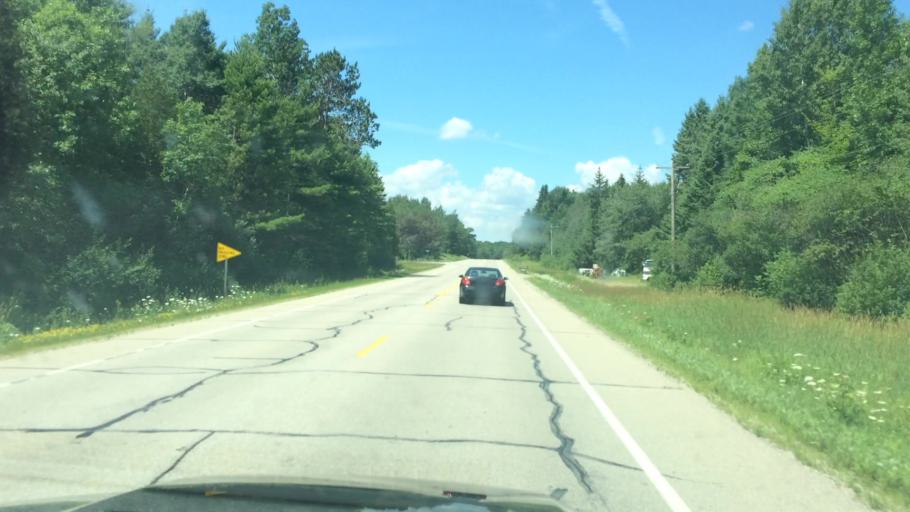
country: US
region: Wisconsin
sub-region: Marinette County
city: Peshtigo
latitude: 45.1002
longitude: -87.7313
